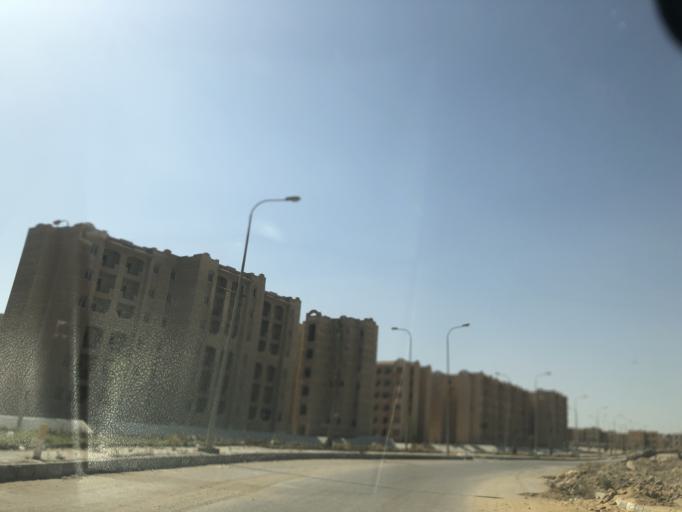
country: EG
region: Al Jizah
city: Madinat Sittah Uktubar
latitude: 29.9257
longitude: 31.0387
